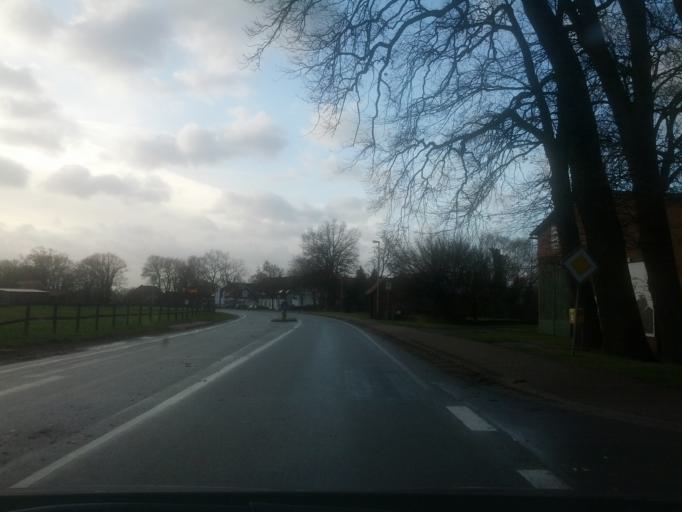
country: DE
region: Lower Saxony
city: Hamersen
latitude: 53.2554
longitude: 9.4828
